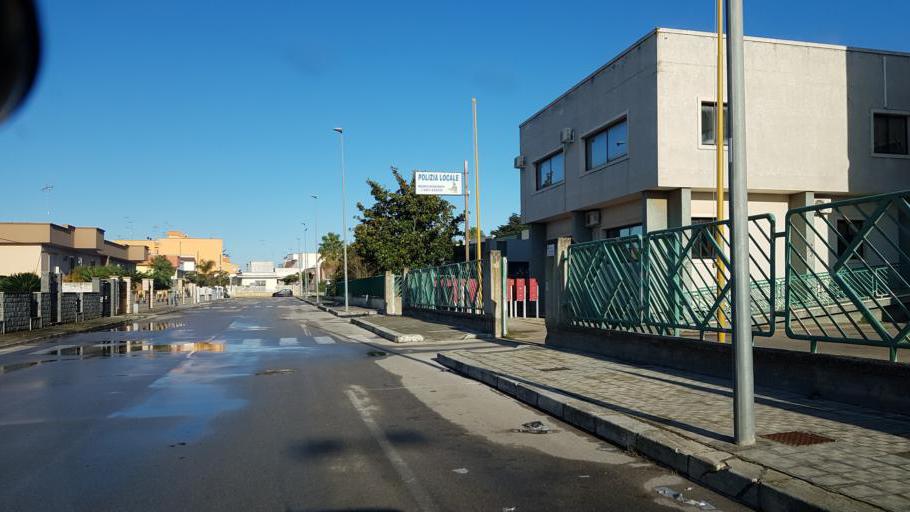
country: IT
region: Apulia
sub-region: Provincia di Brindisi
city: Torchiarolo
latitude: 40.4799
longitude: 18.0556
